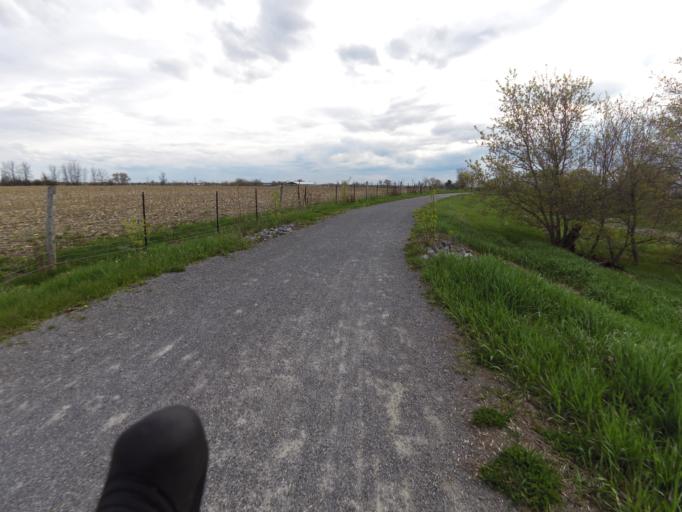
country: CA
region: Ontario
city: Bells Corners
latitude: 45.3077
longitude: -75.7280
